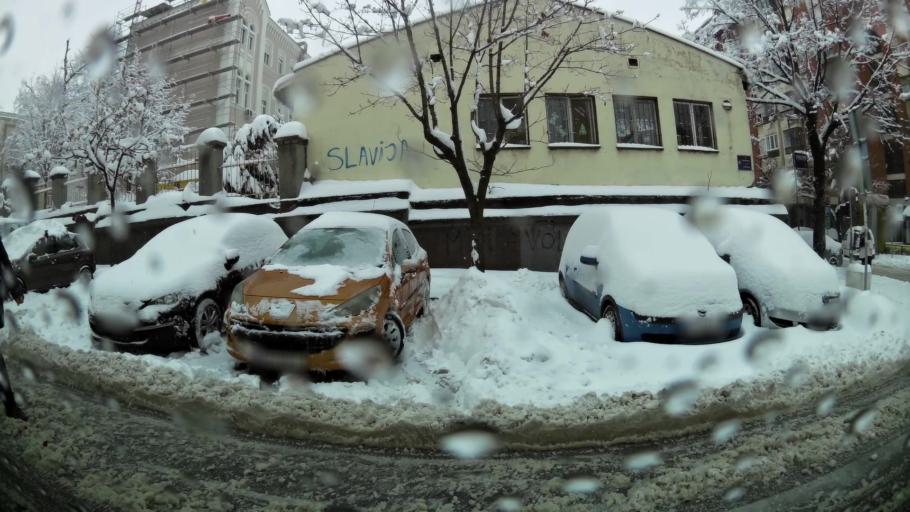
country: RS
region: Central Serbia
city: Belgrade
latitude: 44.8017
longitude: 20.4586
